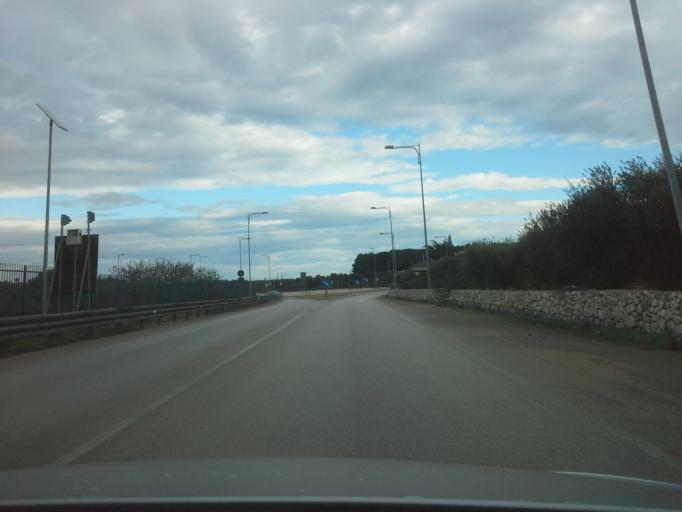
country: IT
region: Apulia
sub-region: Provincia di Bari
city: Turi
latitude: 40.9066
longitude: 17.0273
